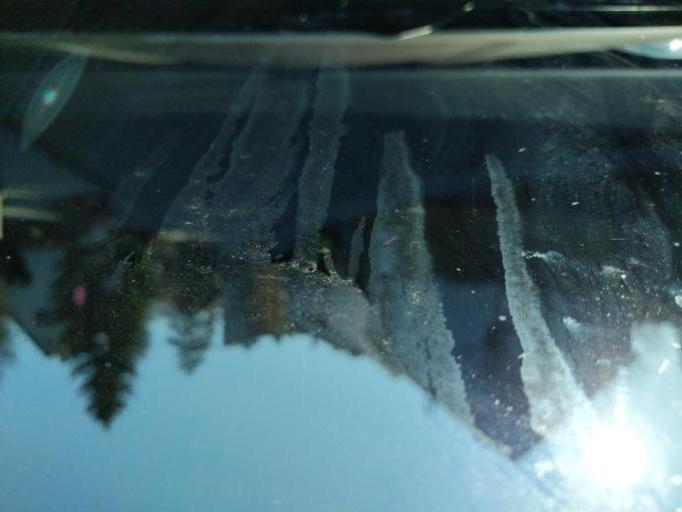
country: DE
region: Bavaria
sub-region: Upper Bavaria
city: Ebersberg
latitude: 48.0736
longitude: 11.9703
